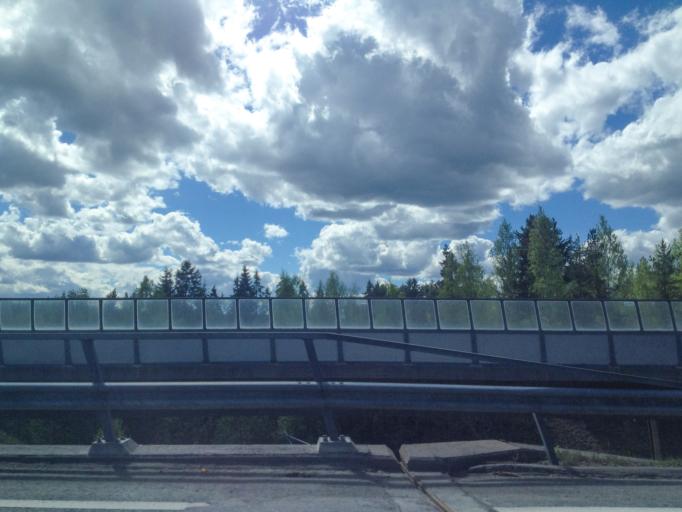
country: FI
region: Haeme
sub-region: Haemeenlinna
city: Parola
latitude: 61.0591
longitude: 24.3398
